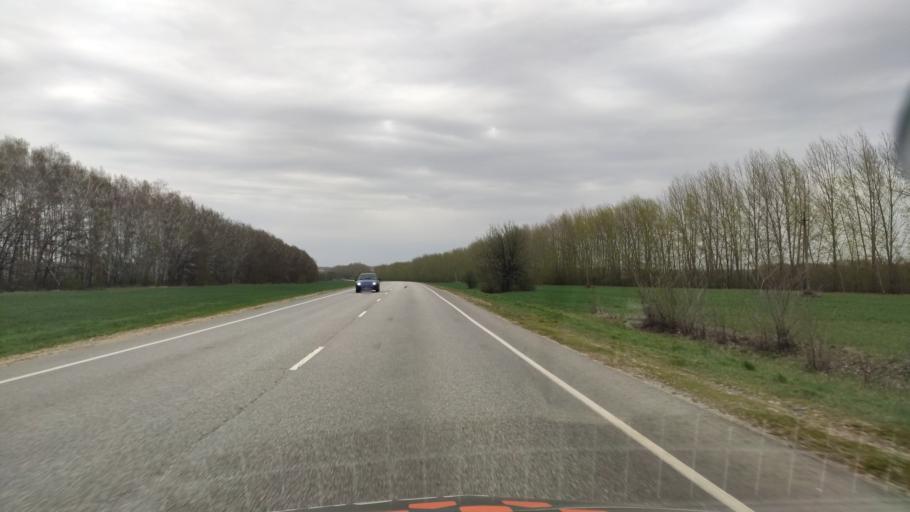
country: RU
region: Kursk
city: Olym
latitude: 51.5511
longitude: 38.2064
